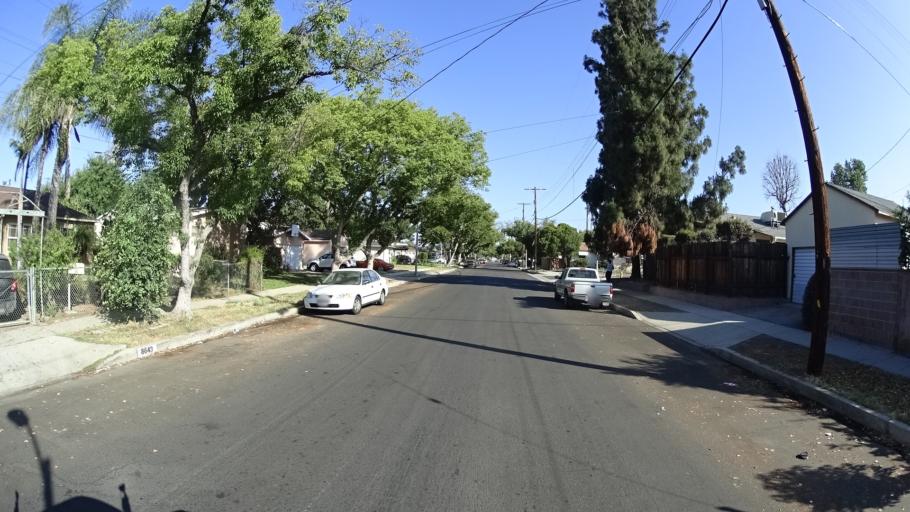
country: US
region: California
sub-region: Los Angeles County
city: Van Nuys
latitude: 34.2270
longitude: -118.4204
